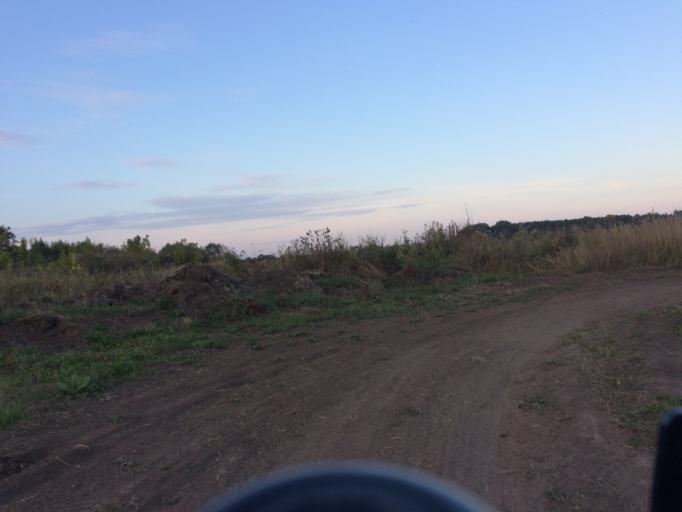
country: RU
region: Mariy-El
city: Yoshkar-Ola
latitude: 56.6459
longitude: 47.9189
